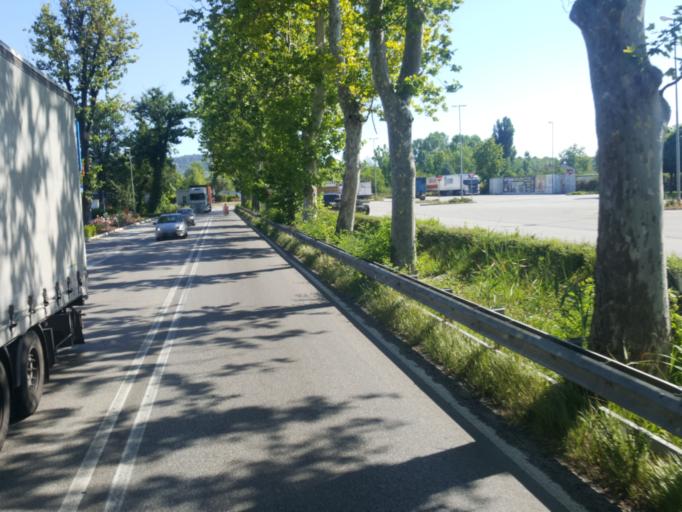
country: IT
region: The Marches
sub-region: Provincia di Pesaro e Urbino
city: Villa Ceccolini
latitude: 43.8894
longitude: 12.8322
